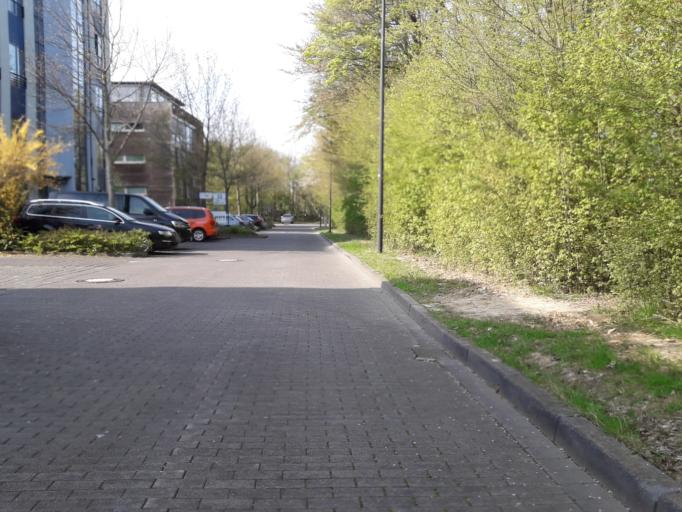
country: DE
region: North Rhine-Westphalia
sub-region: Regierungsbezirk Detmold
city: Paderborn
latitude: 51.7014
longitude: 8.7672
